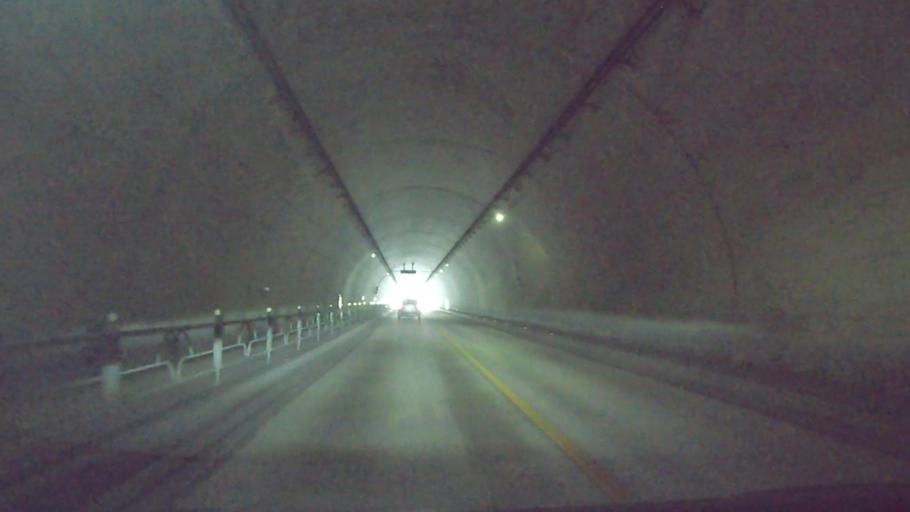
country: JP
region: Tokyo
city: Itsukaichi
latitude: 35.7146
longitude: 139.2320
